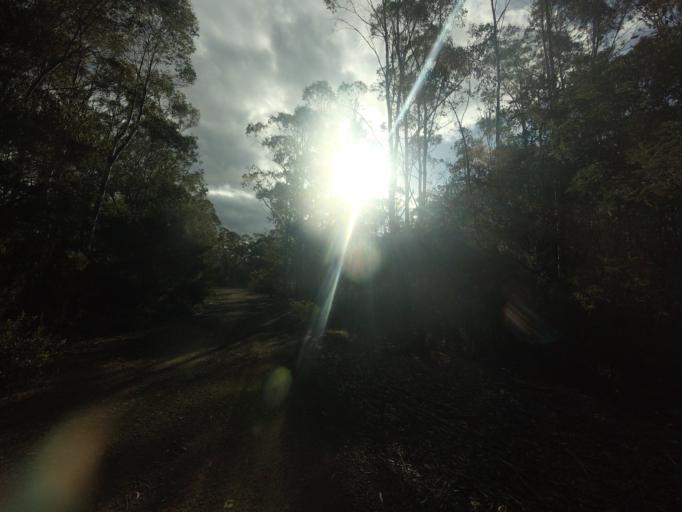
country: AU
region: Tasmania
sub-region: Break O'Day
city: St Helens
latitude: -41.8487
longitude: 148.0495
